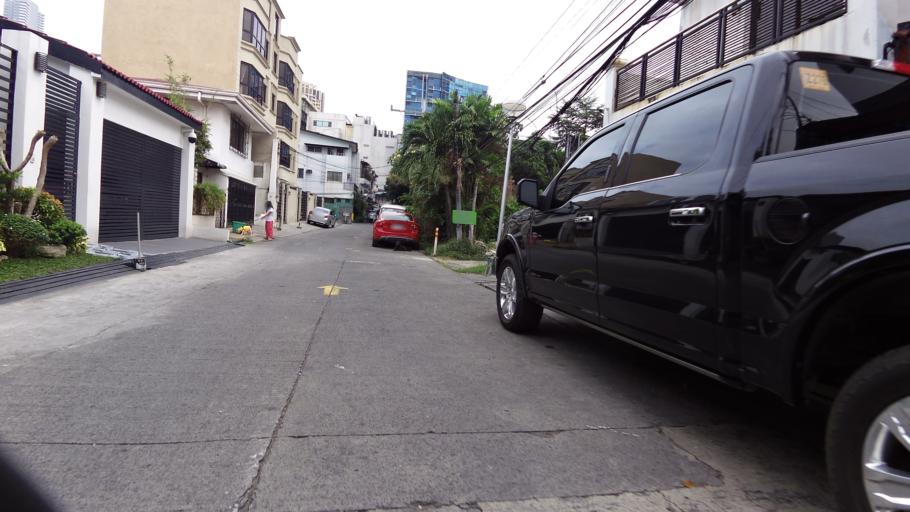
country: PH
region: Metro Manila
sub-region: Pasig
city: Pasig City
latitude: 14.5697
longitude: 121.0647
